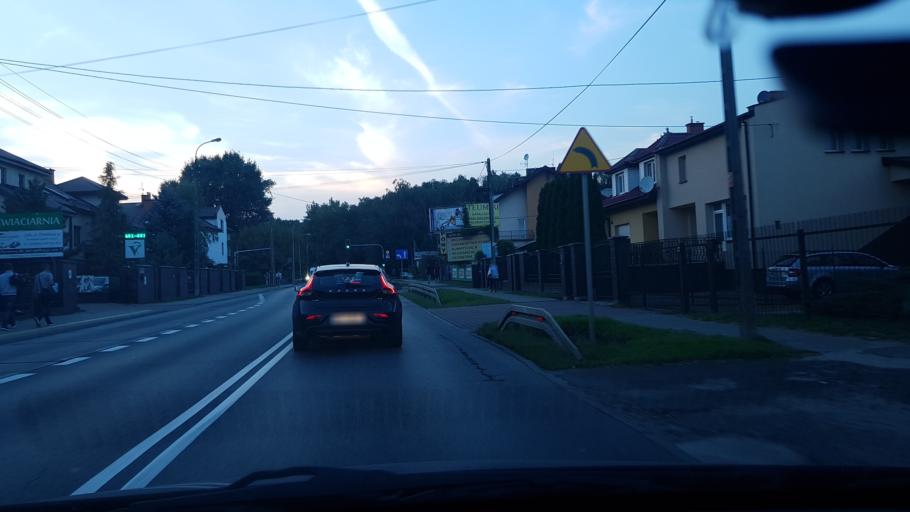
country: PL
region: Masovian Voivodeship
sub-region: Warszawa
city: Targowek
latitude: 52.2907
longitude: 21.0699
